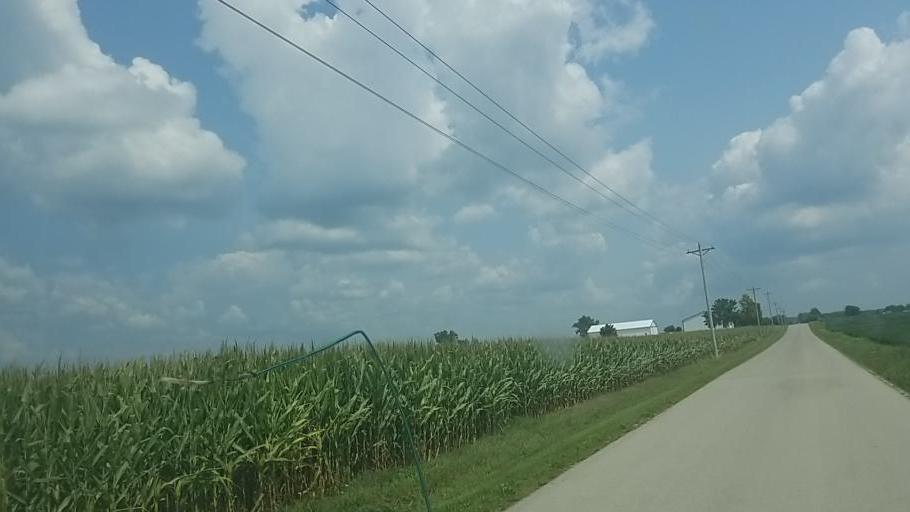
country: US
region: Ohio
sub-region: Wyandot County
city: Upper Sandusky
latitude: 40.9209
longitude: -83.1637
